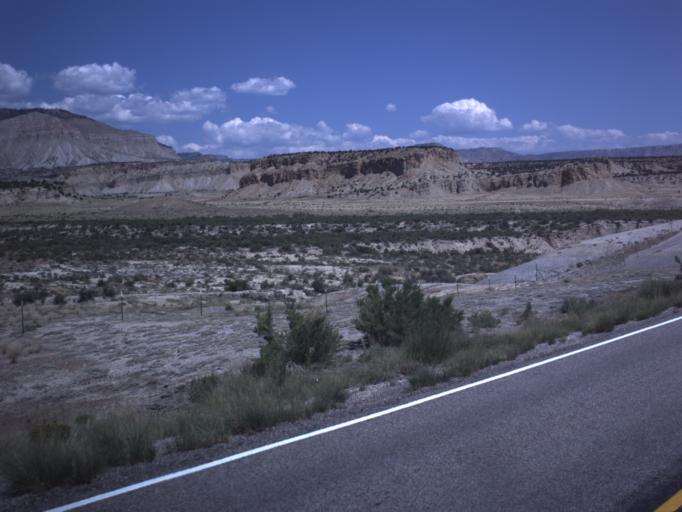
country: US
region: Utah
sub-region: Emery County
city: Ferron
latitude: 38.8101
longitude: -111.3353
